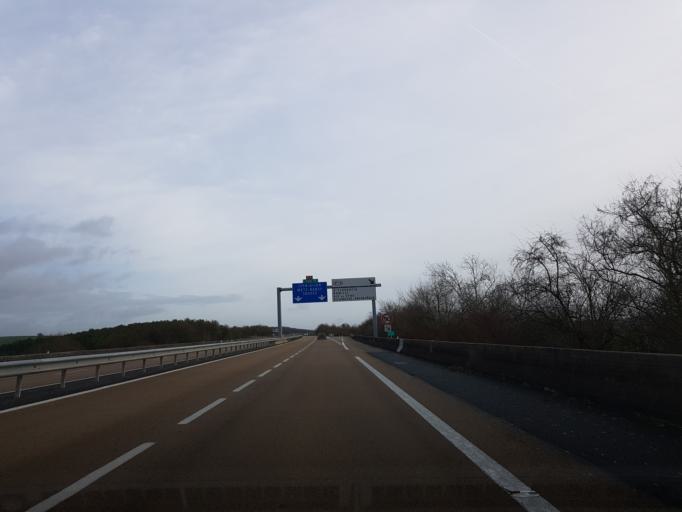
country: FR
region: Champagne-Ardenne
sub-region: Departement de l'Aube
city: Aix-en-Othe
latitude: 48.2404
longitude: 3.5940
